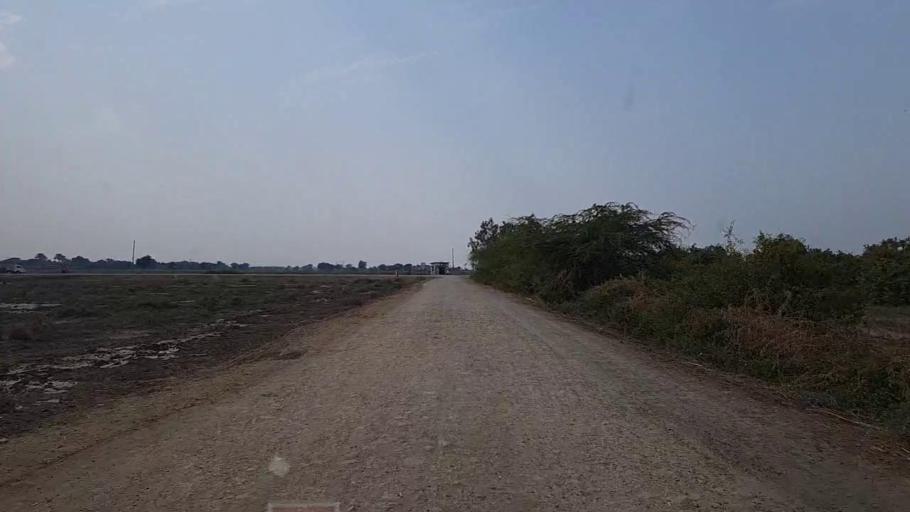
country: PK
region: Sindh
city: Mirwah Gorchani
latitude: 25.3370
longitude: 69.0396
